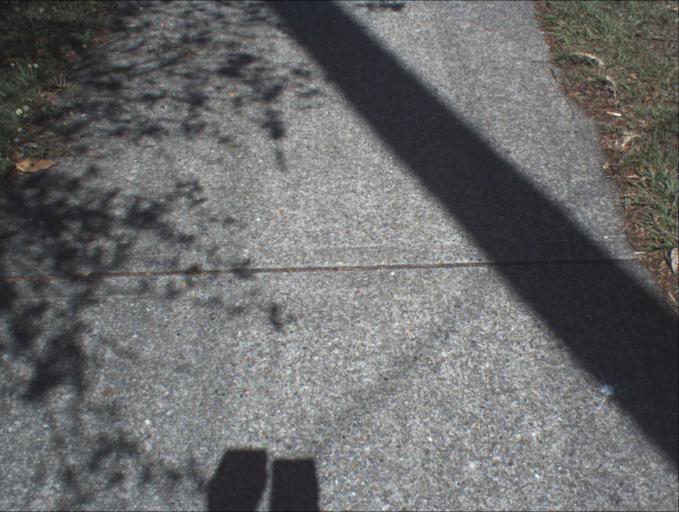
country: AU
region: Queensland
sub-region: Logan
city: Windaroo
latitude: -27.7231
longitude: 153.2040
